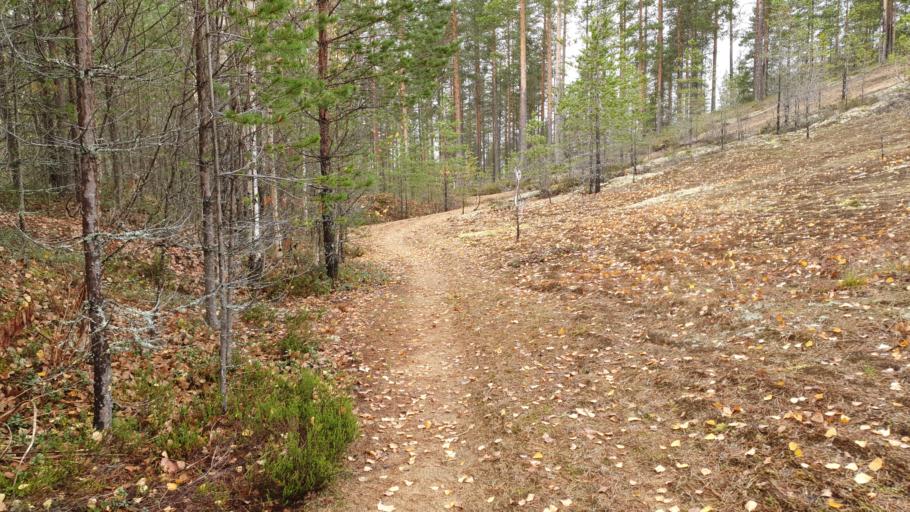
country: FI
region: Kainuu
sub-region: Kehys-Kainuu
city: Kuhmo
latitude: 64.1489
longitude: 29.4080
